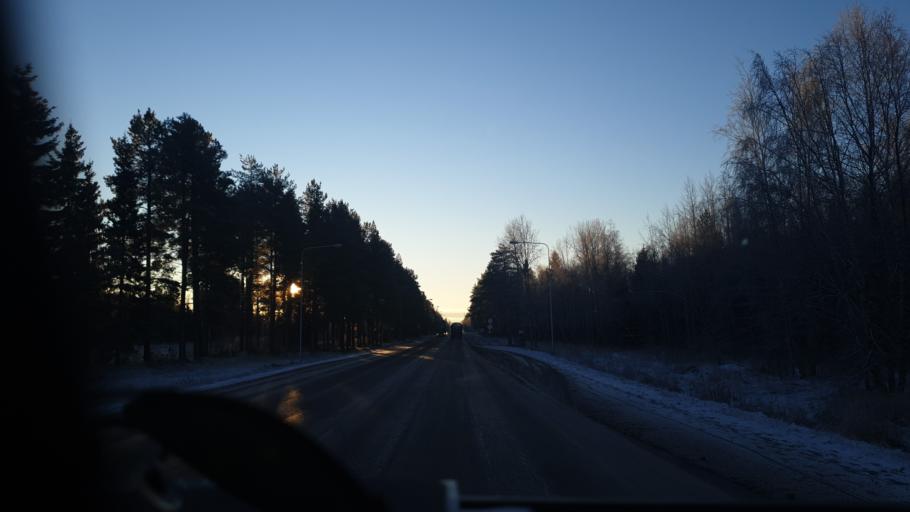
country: FI
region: Northern Ostrobothnia
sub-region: Ylivieska
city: Kalajoki
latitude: 64.2777
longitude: 23.9487
